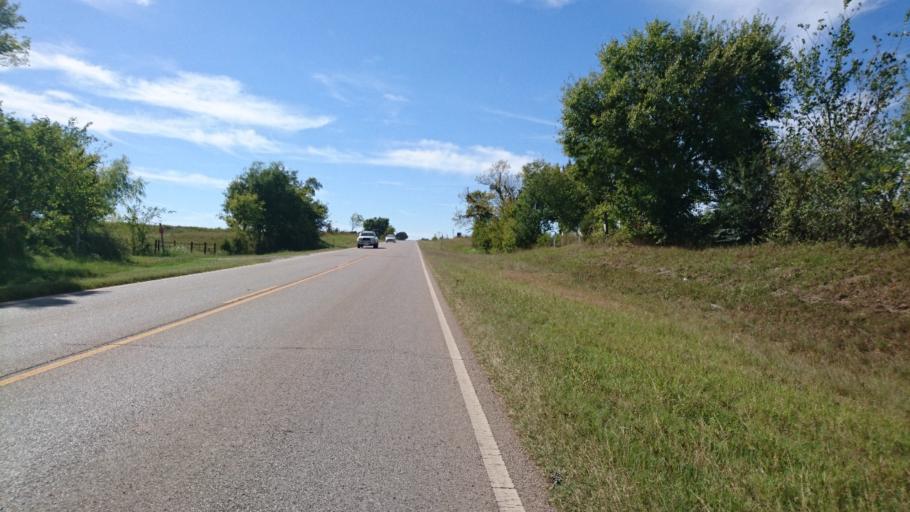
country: US
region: Oklahoma
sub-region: Lincoln County
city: Chandler
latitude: 35.7099
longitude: -96.7791
